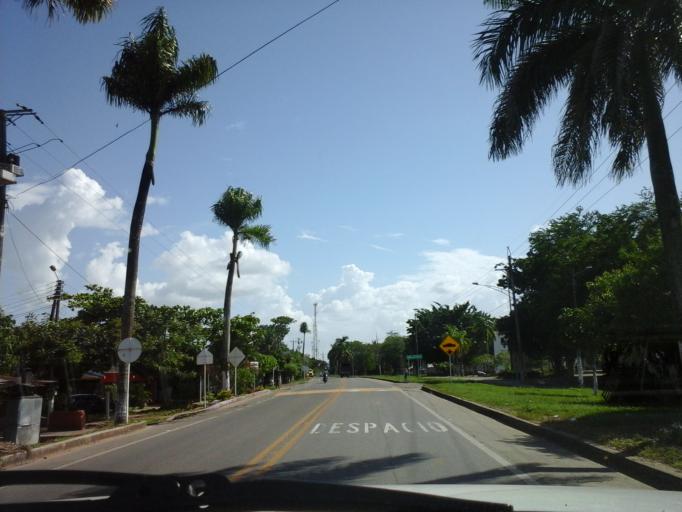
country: CO
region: Meta
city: Puerto Lopez
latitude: 4.0917
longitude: -72.9558
